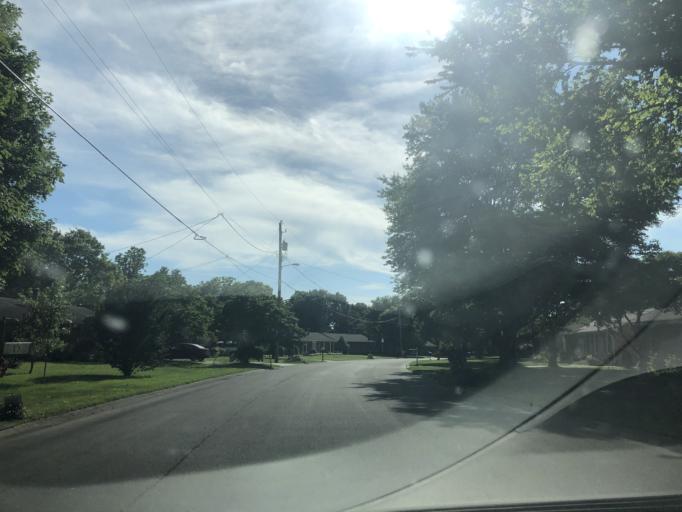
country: US
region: Tennessee
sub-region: Davidson County
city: Belle Meade
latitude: 36.0681
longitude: -86.9367
